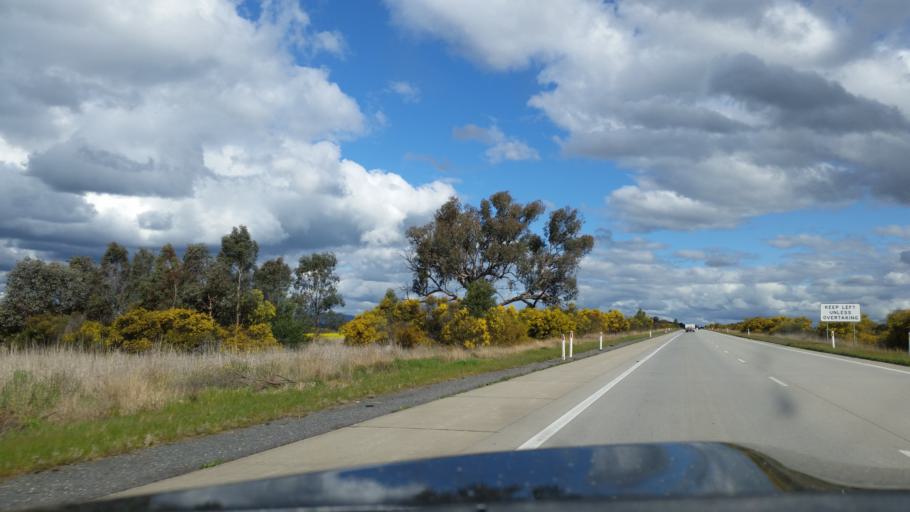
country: AU
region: New South Wales
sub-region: Greater Hume Shire
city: Jindera
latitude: -35.9518
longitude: 147.0043
